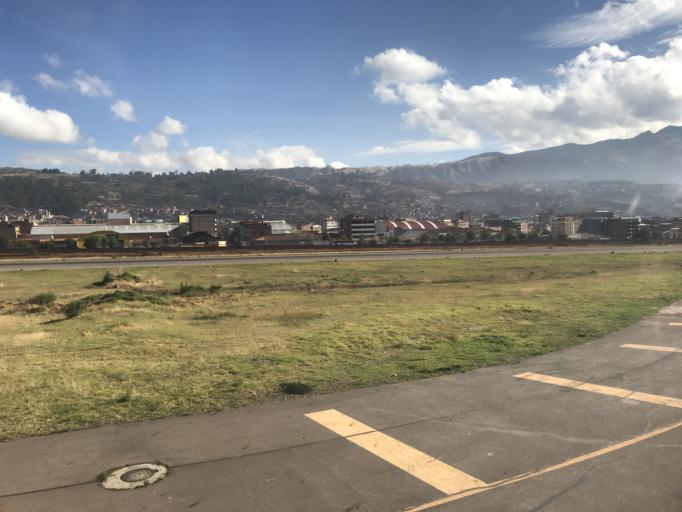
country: PE
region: Cusco
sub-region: Provincia de Cusco
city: Cusco
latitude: -13.5367
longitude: -71.9421
